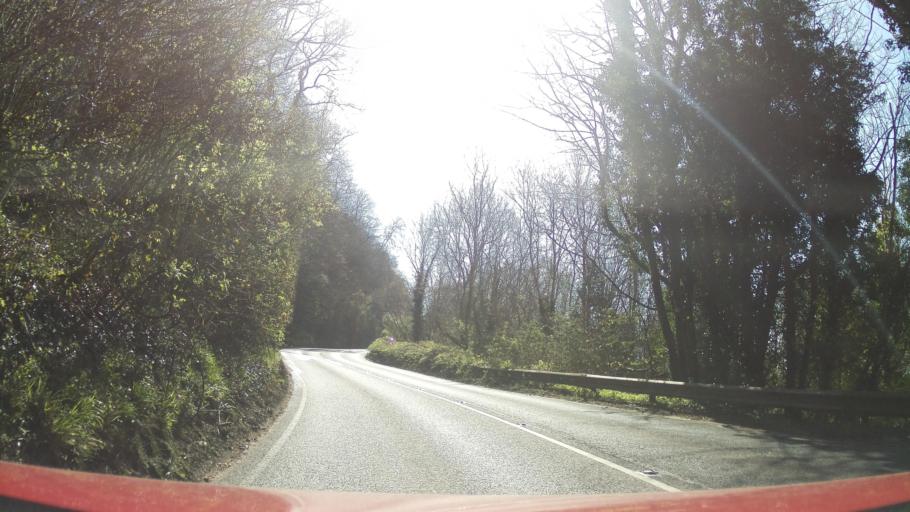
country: GB
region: England
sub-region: Bath and North East Somerset
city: Freshford
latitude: 51.3850
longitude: -2.3016
